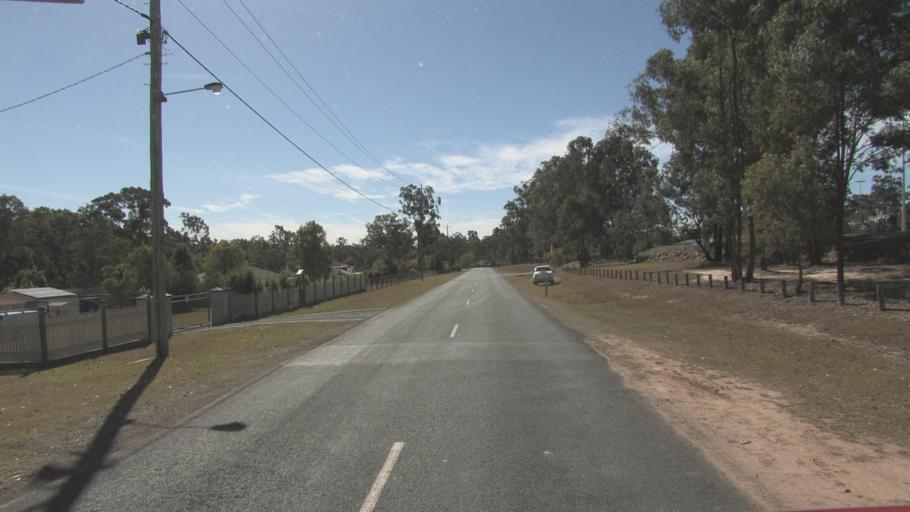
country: AU
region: Queensland
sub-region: Logan
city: North Maclean
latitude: -27.7287
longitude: 152.9617
